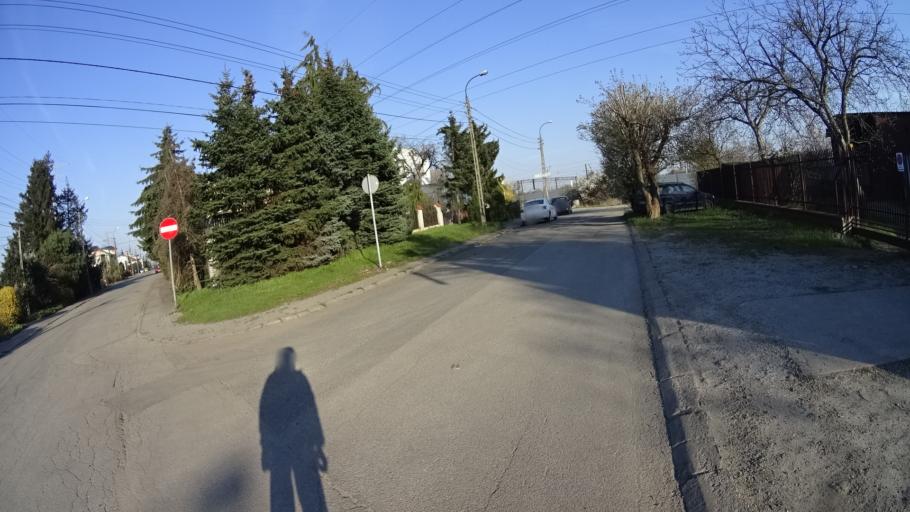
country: PL
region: Masovian Voivodeship
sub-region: Warszawa
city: Ursus
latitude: 52.2161
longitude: 20.9029
